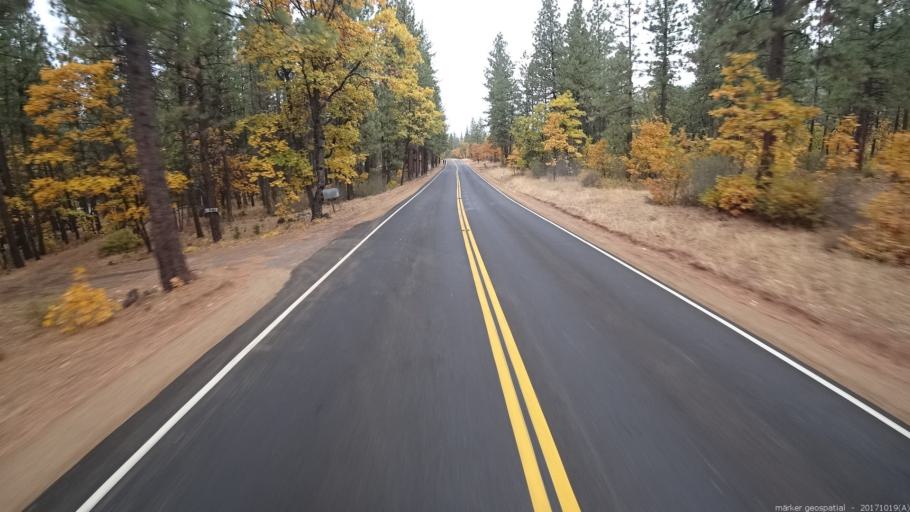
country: US
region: California
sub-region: Shasta County
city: Burney
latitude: 41.1599
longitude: -121.3566
